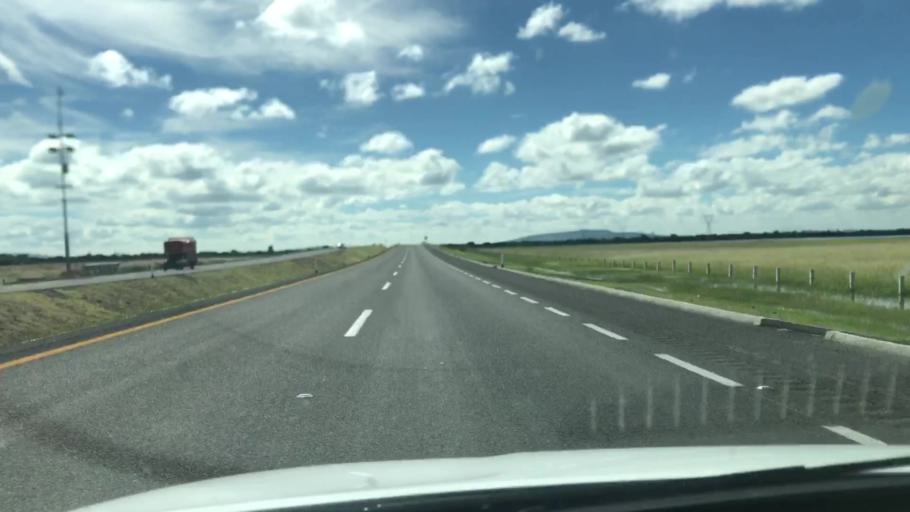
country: MX
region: Guanajuato
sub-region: Silao de la Victoria
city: La Aldea
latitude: 20.8585
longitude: -101.4633
